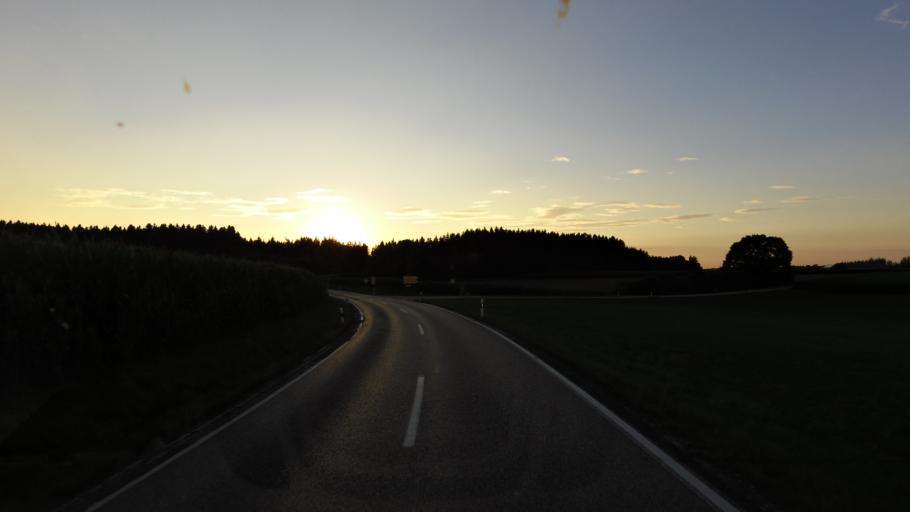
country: DE
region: Bavaria
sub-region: Upper Bavaria
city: Trostberg an der Alz
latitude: 48.0398
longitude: 12.5217
